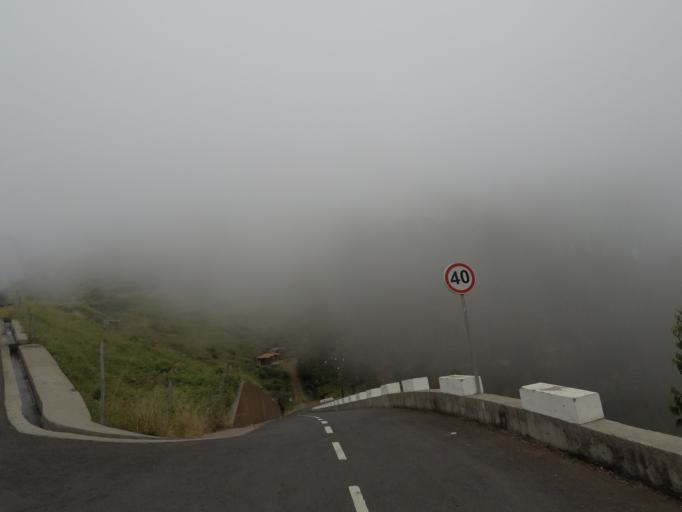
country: PT
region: Madeira
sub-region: Camara de Lobos
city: Curral das Freiras
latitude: 32.6903
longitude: -16.9473
